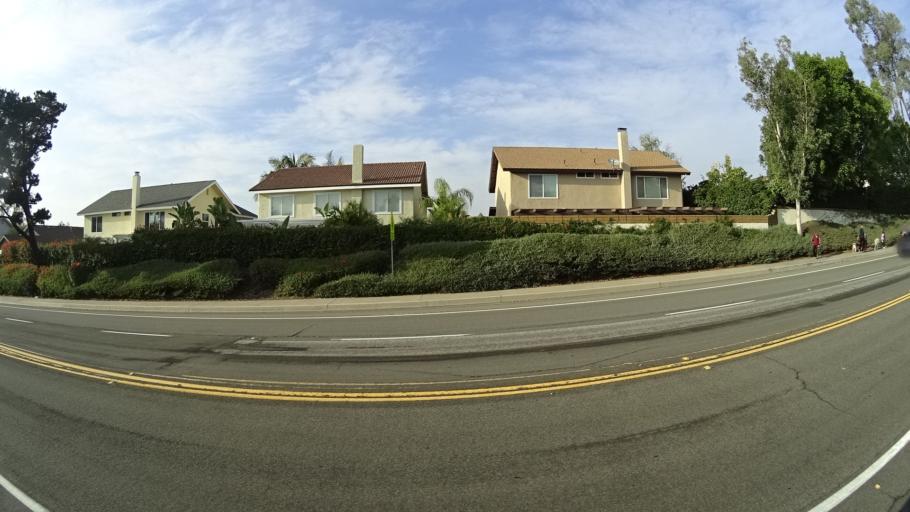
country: US
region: California
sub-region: Orange County
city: Lake Forest
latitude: 33.6401
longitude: -117.6866
